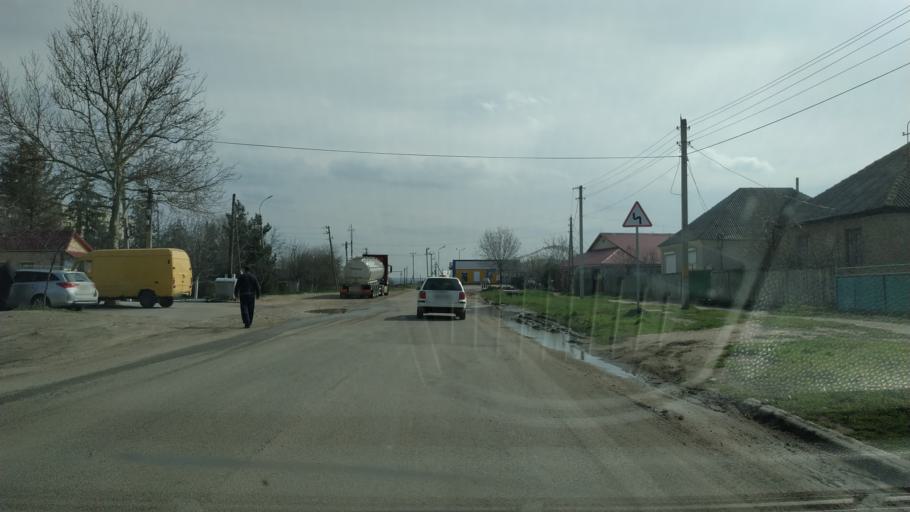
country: MD
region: Gagauzia
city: Vulcanesti
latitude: 45.6781
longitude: 28.4107
